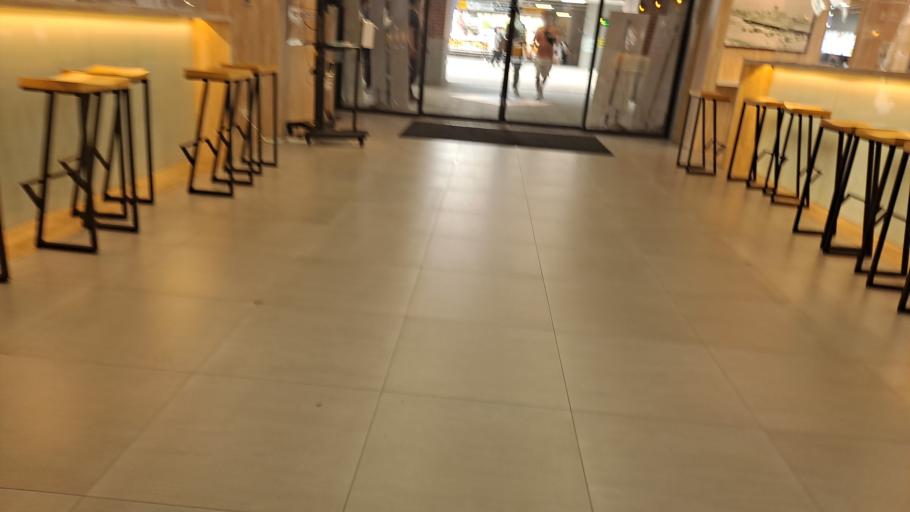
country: TW
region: Taiwan
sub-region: Taichung City
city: Taichung
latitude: 24.1370
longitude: 120.6867
